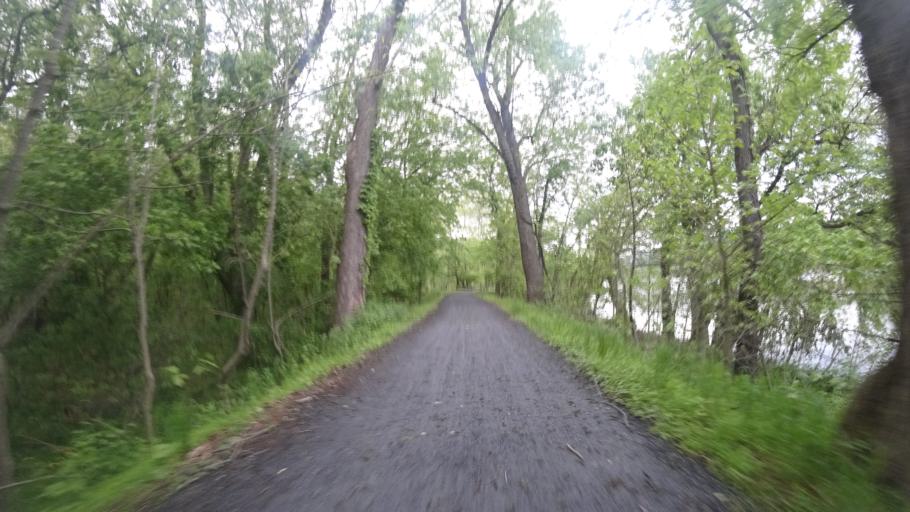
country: US
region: West Virginia
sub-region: Jefferson County
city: Bolivar
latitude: 39.3363
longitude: -77.7529
